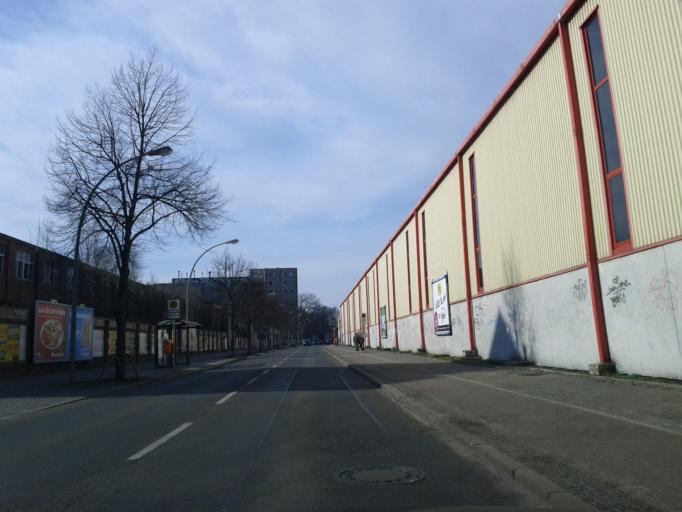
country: DE
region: Berlin
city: Berlin Koepenick
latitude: 52.4514
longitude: 13.5898
